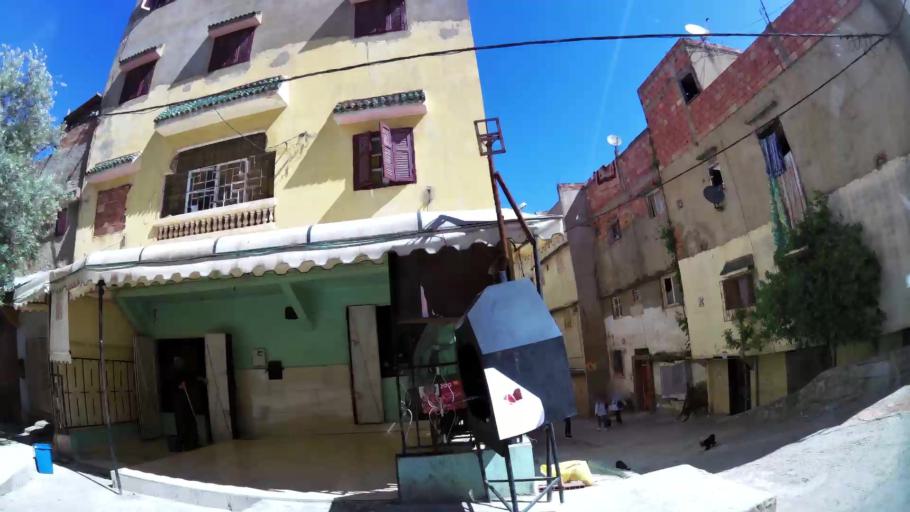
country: MA
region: Meknes-Tafilalet
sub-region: Meknes
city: Meknes
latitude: 33.9091
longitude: -5.5384
